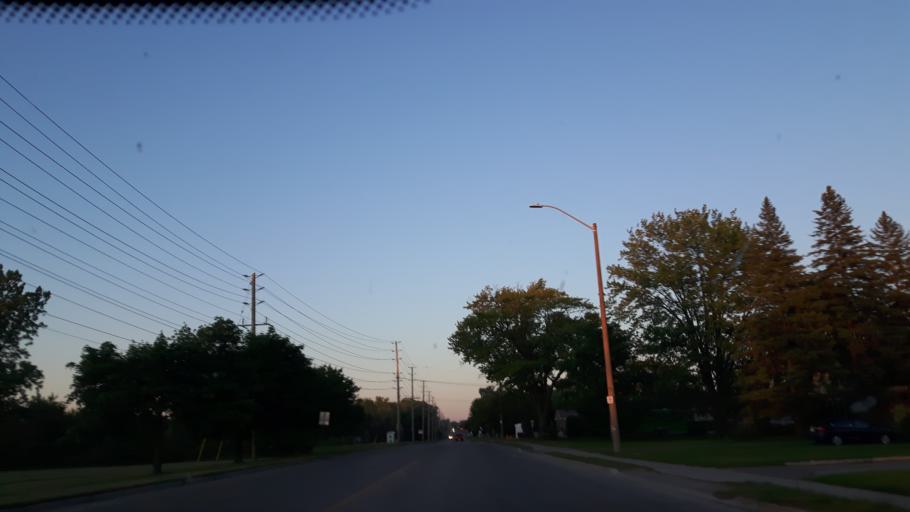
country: CA
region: Ontario
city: London
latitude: 42.9438
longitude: -81.2227
